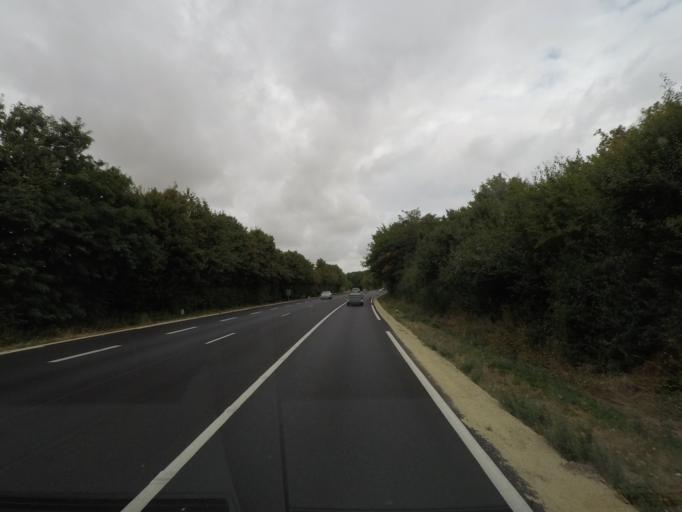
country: FR
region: Poitou-Charentes
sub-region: Departement des Deux-Sevres
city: Celles-sur-Belle
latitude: 46.2601
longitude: -0.2276
